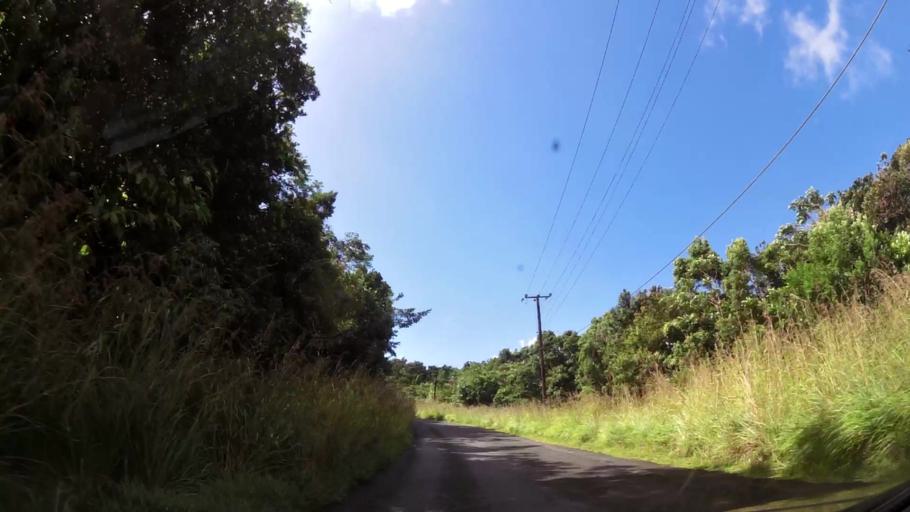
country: DM
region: Saint Paul
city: Pont Casse
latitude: 15.3864
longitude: -61.3369
